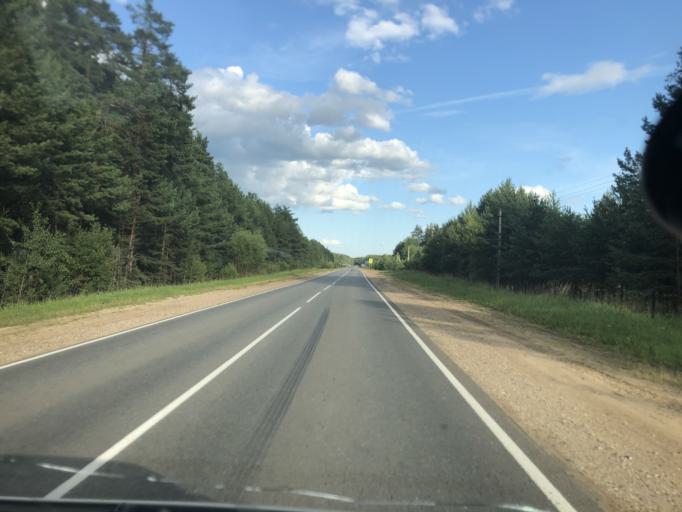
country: RU
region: Kaluga
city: Yukhnov
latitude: 54.7216
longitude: 35.2198
